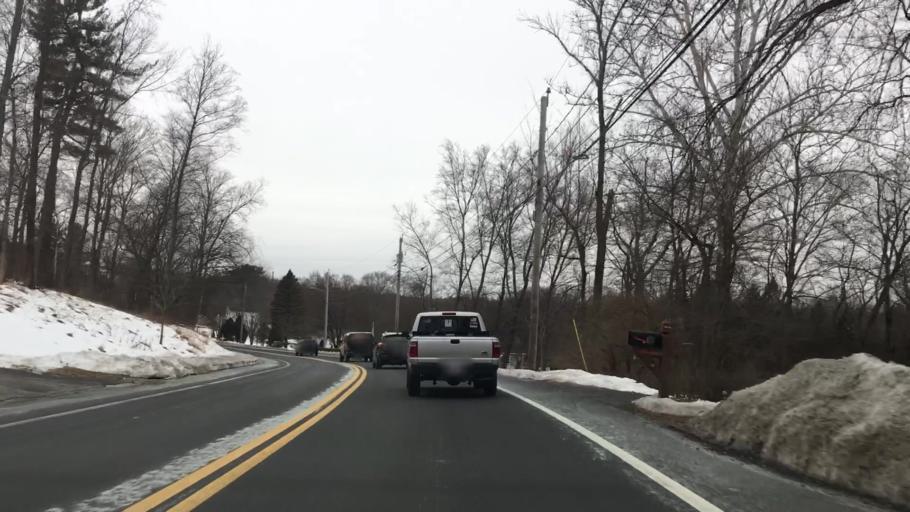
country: US
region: Massachusetts
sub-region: Hampden County
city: Westfield
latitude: 42.1044
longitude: -72.7034
